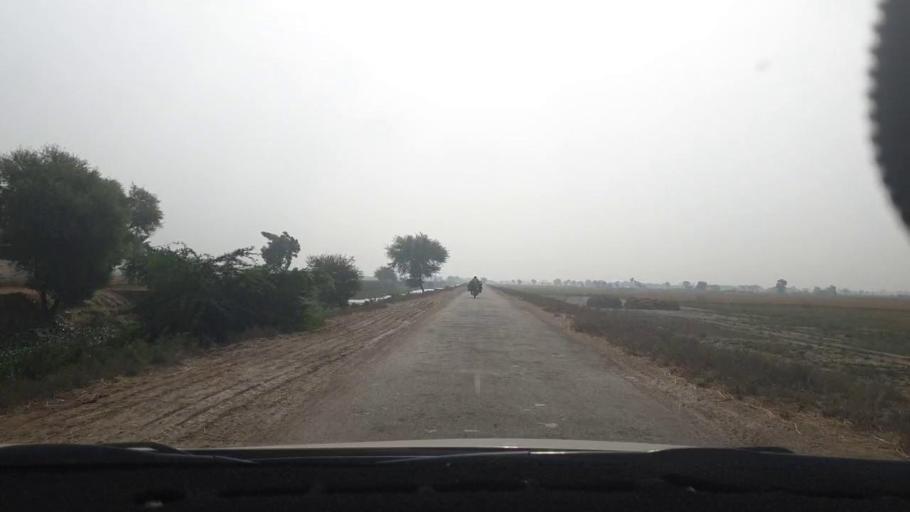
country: PK
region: Sindh
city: Tando Muhammad Khan
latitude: 25.0757
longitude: 68.5342
